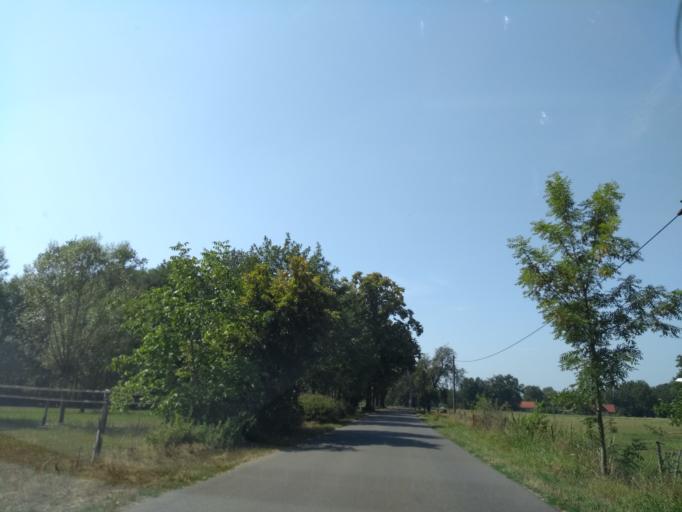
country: DE
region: Brandenburg
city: Burg
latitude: 51.8443
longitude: 14.1396
